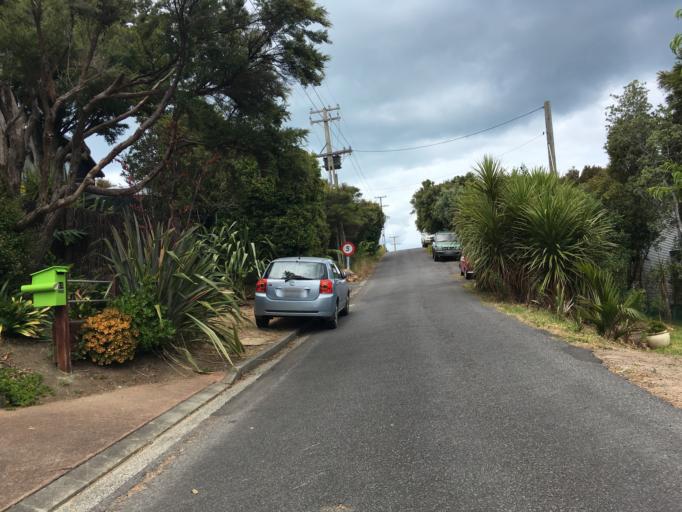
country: NZ
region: Auckland
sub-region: Auckland
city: Pakuranga
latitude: -36.7889
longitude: 175.0208
